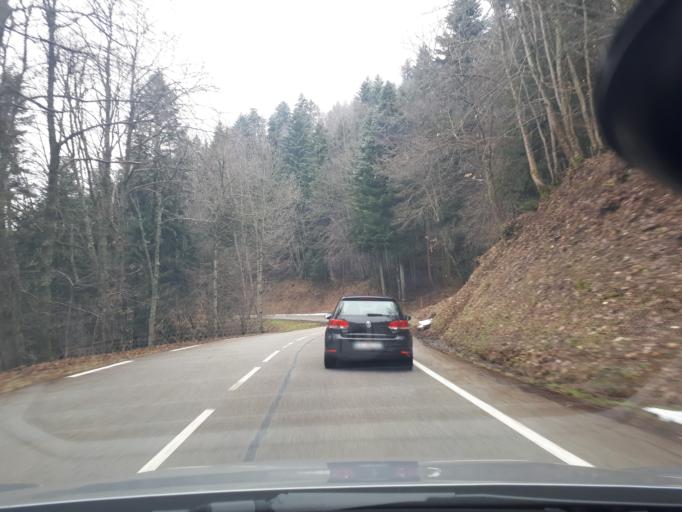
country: FR
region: Rhone-Alpes
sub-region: Departement de l'Isere
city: Vaulnaveys-le-Bas
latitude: 45.1172
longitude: 5.8406
